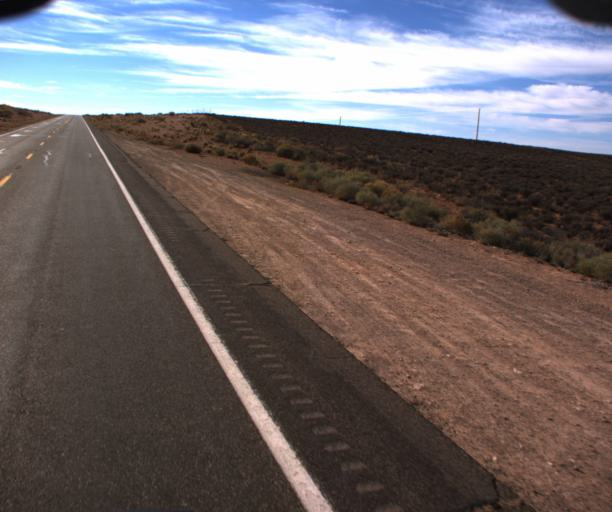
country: US
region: Arizona
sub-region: Coconino County
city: LeChee
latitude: 36.8022
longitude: -111.3038
